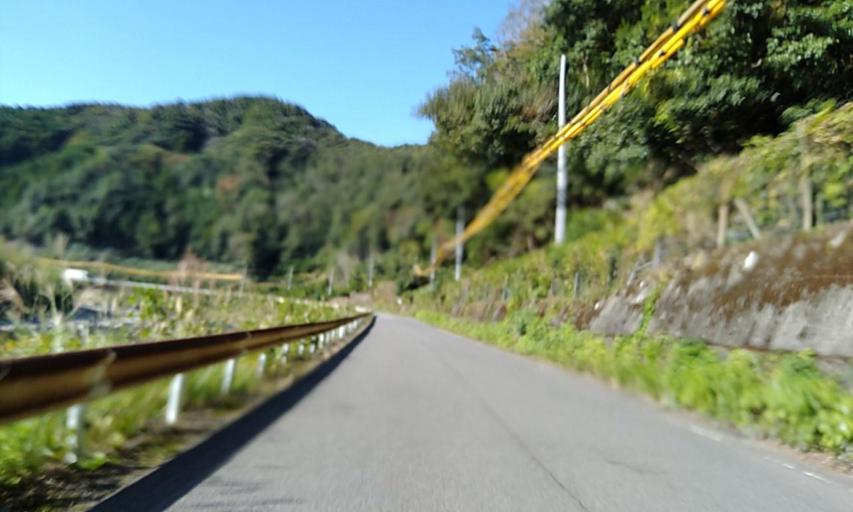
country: JP
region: Wakayama
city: Kainan
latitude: 34.0532
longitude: 135.3166
